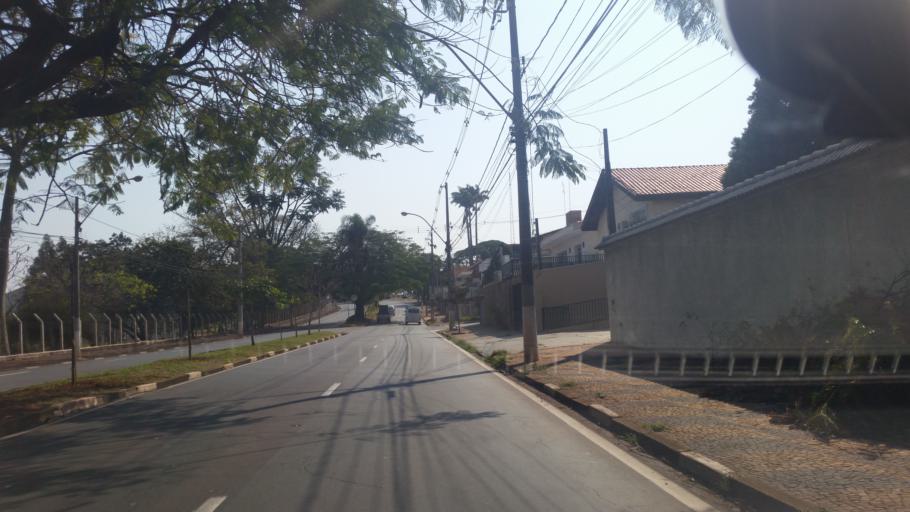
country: BR
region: Sao Paulo
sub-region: Campinas
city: Campinas
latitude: -22.8834
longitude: -47.0765
